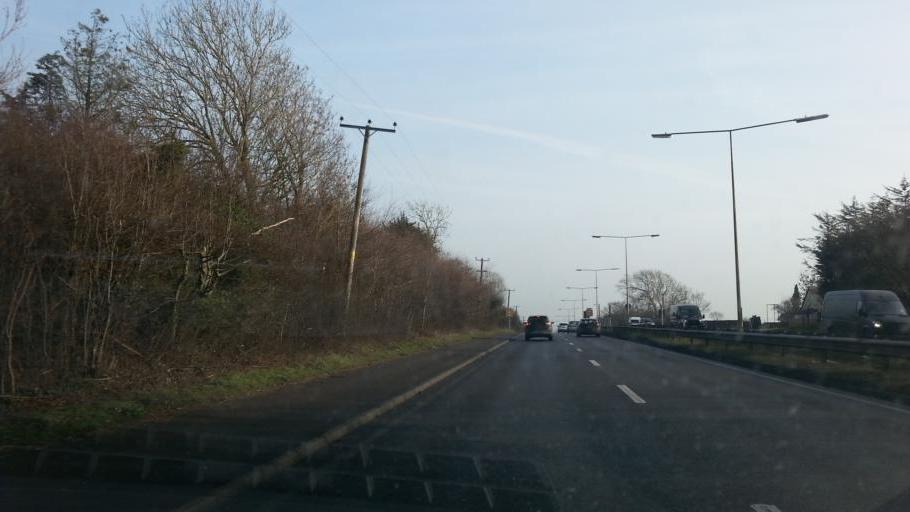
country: GB
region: England
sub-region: Essex
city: Wickford
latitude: 51.5897
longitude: 0.5414
